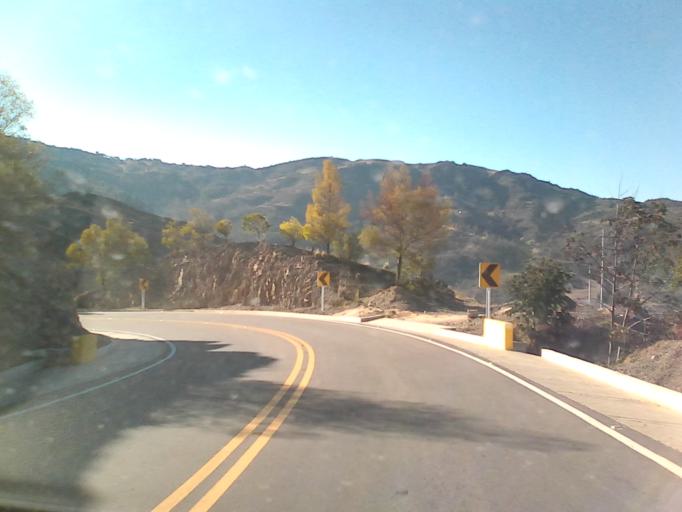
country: CO
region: Boyaca
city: Cucaita
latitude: 5.5477
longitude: -73.4467
